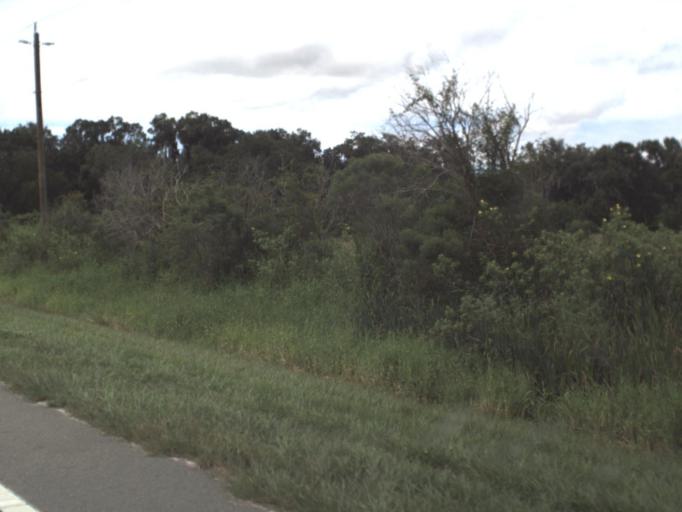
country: US
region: Florida
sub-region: Manatee County
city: Ellenton
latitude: 27.5875
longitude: -82.4142
